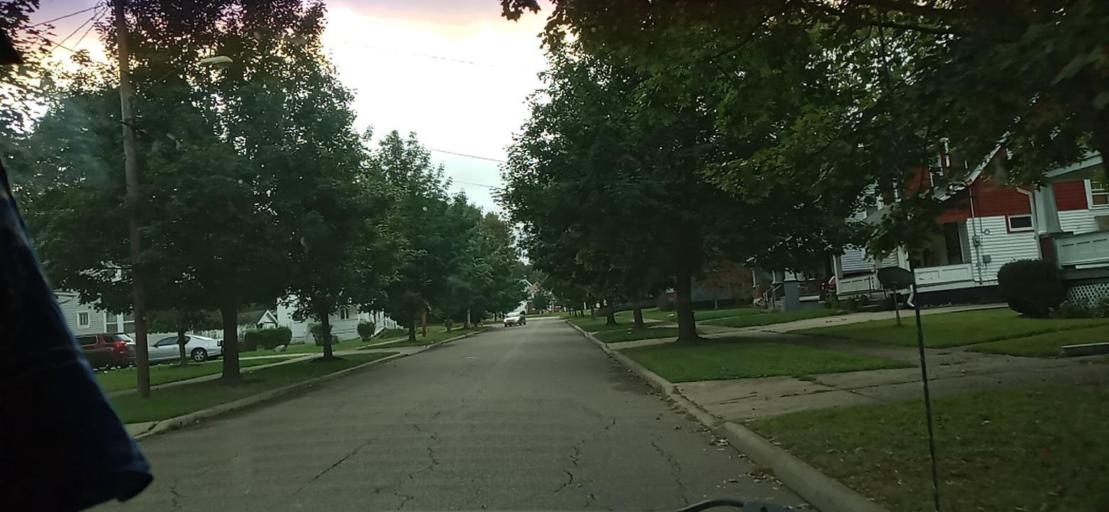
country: US
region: Ohio
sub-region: Summit County
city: Akron
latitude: 41.0805
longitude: -81.5508
